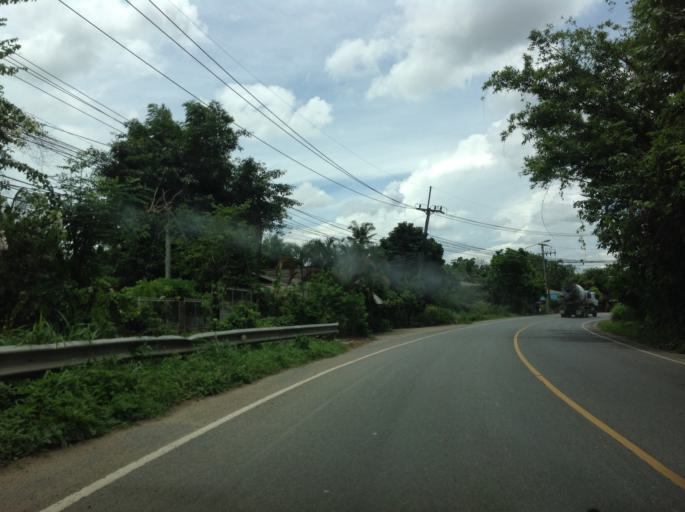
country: TH
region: Chiang Mai
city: Hang Dong
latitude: 18.7351
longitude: 98.9043
